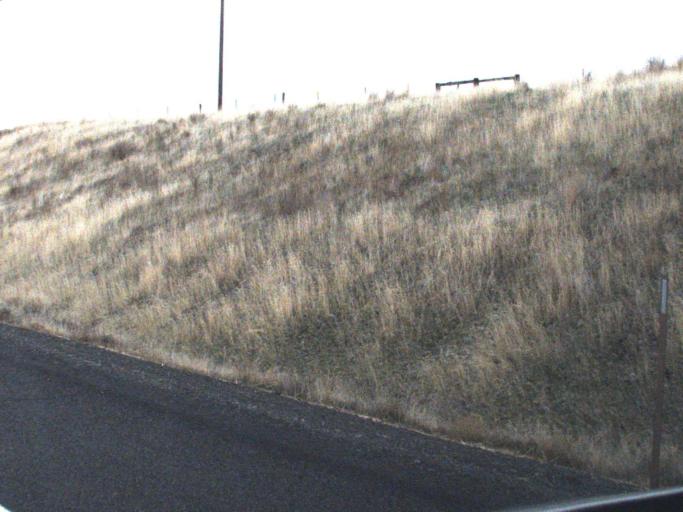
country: US
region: Washington
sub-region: Columbia County
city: Dayton
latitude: 46.7701
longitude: -118.0354
